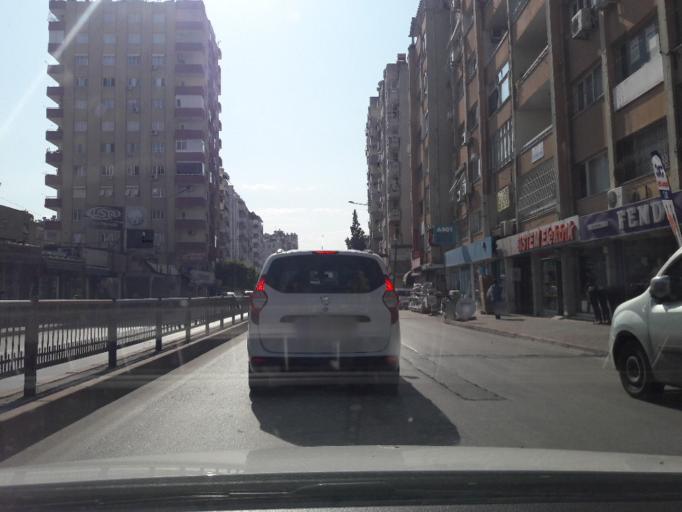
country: TR
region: Adana
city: Adana
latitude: 37.0112
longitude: 35.3232
